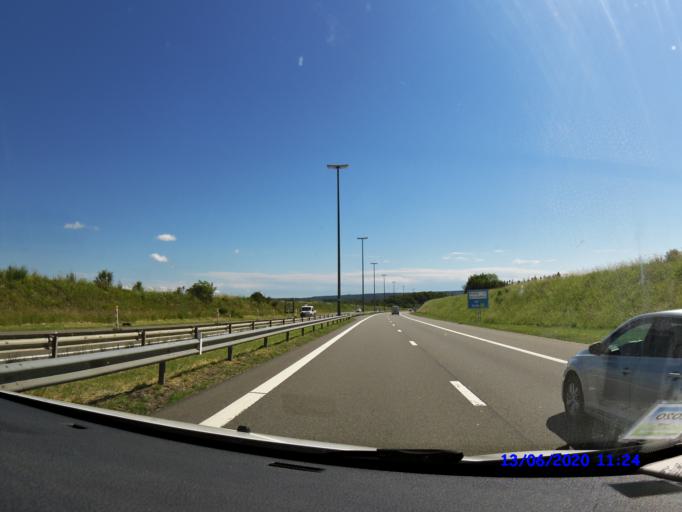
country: BE
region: Wallonia
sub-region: Province de Liege
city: Spa
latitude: 50.5269
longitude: 5.9065
